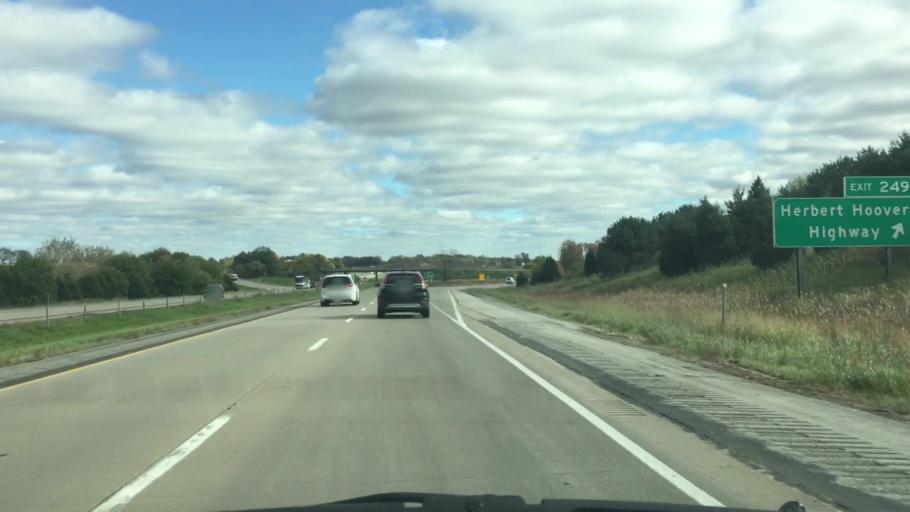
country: US
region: Iowa
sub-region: Johnson County
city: Iowa City
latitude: 41.6736
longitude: -91.4512
